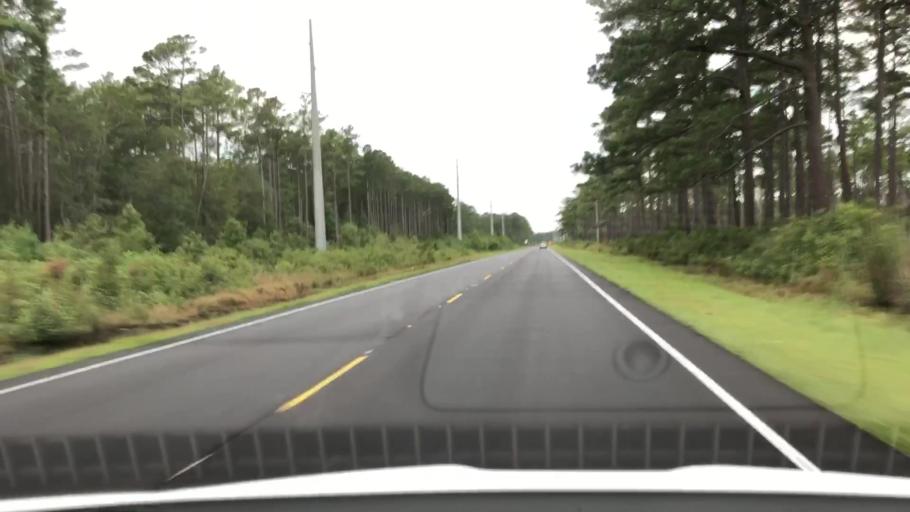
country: US
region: North Carolina
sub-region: Onslow County
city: Swansboro
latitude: 34.7774
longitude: -77.1034
